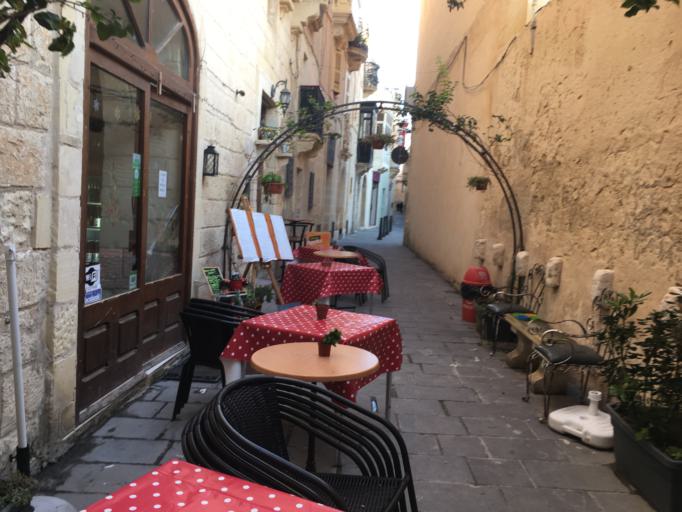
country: MT
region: Ir-Rabat
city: Rabat
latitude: 35.8836
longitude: 14.4005
